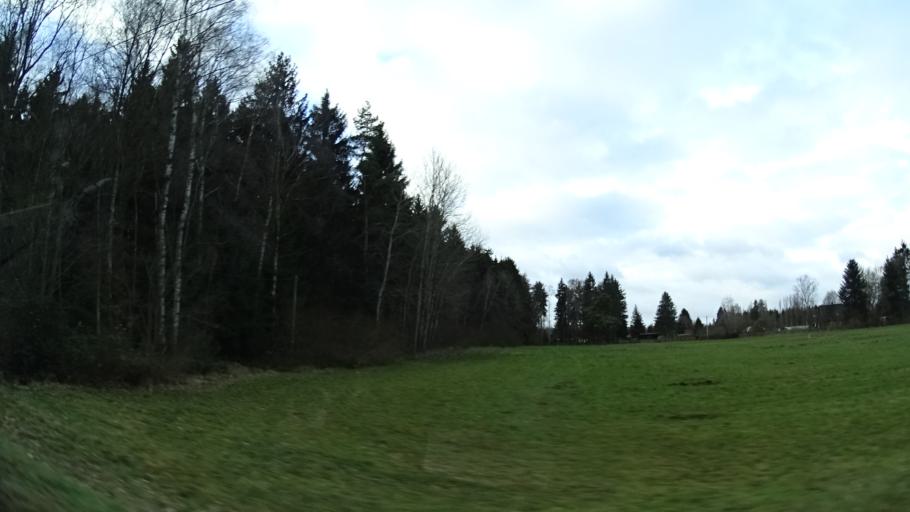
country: DE
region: Thuringia
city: Zeulenroda
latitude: 50.6267
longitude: 11.9989
